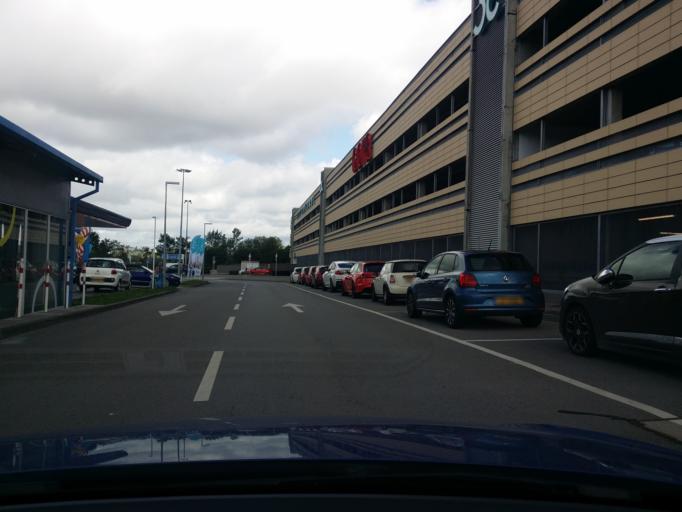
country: LU
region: Luxembourg
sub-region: Canton de Luxembourg
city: Bertrange
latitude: 49.6011
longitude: 6.0628
